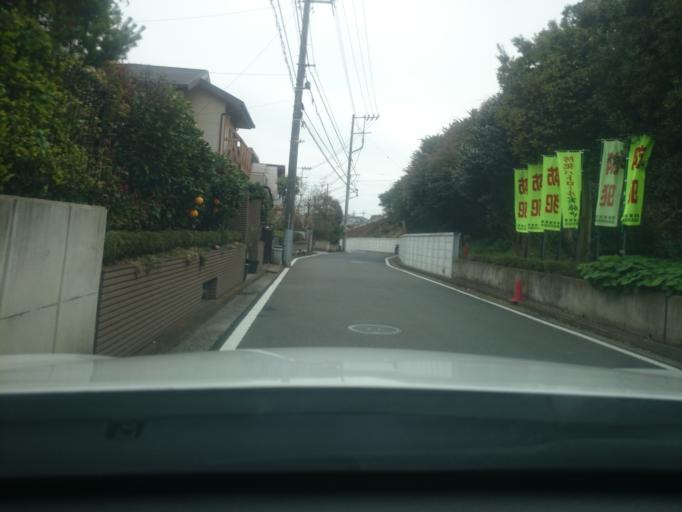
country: JP
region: Tokyo
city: Chofugaoka
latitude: 35.5657
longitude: 139.5753
